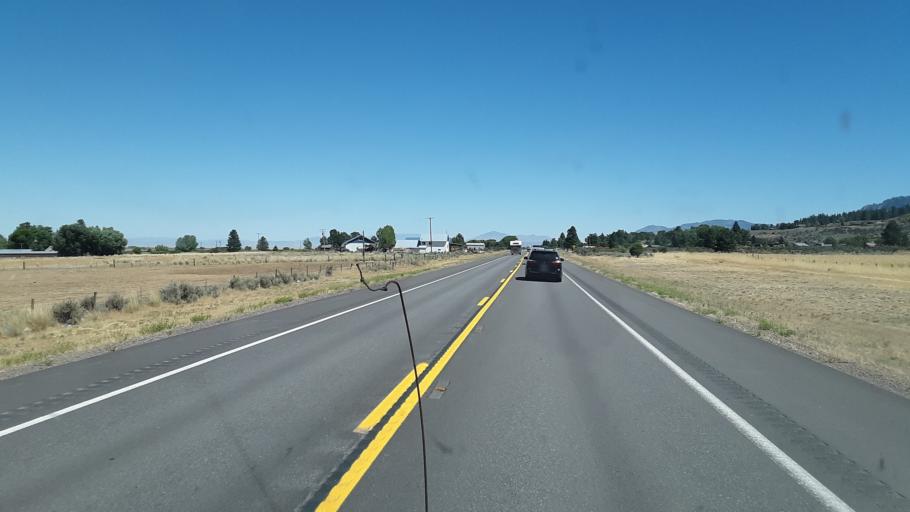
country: US
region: California
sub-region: Lassen County
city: Janesville
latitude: 40.2970
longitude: -120.5130
